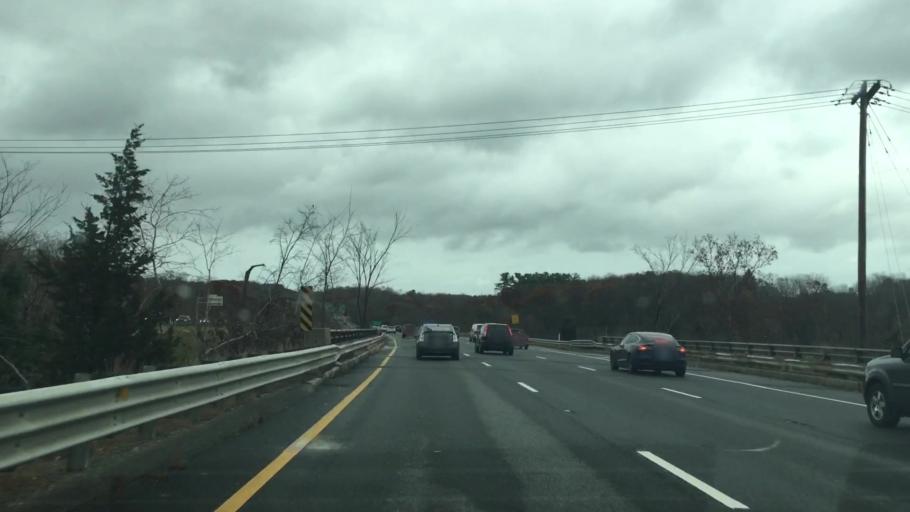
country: US
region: Massachusetts
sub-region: Essex County
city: Amesbury
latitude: 42.8422
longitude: -70.9273
